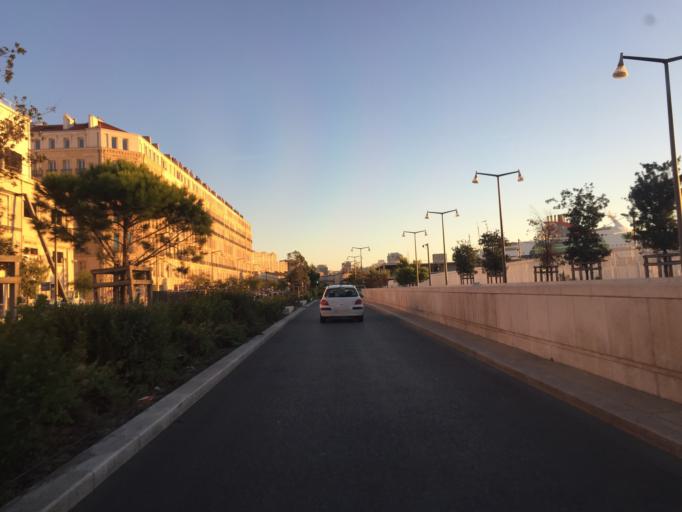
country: FR
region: Provence-Alpes-Cote d'Azur
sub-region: Departement des Bouches-du-Rhone
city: Marseille 02
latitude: 43.3031
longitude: 5.3647
